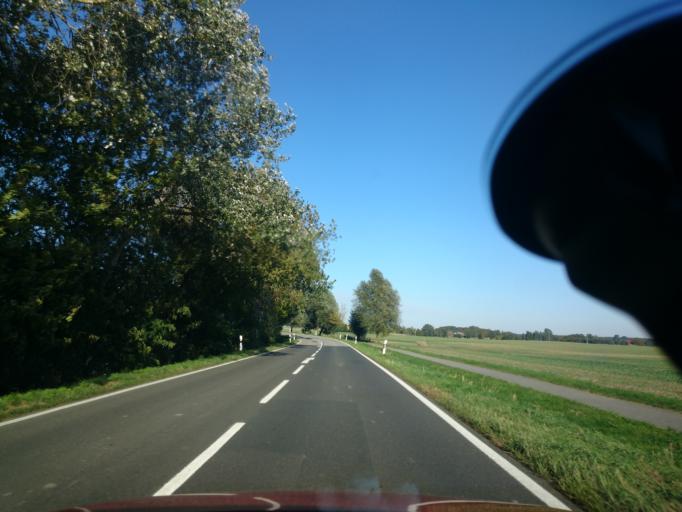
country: DE
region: Mecklenburg-Vorpommern
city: Saal
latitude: 54.3264
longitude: 12.5132
